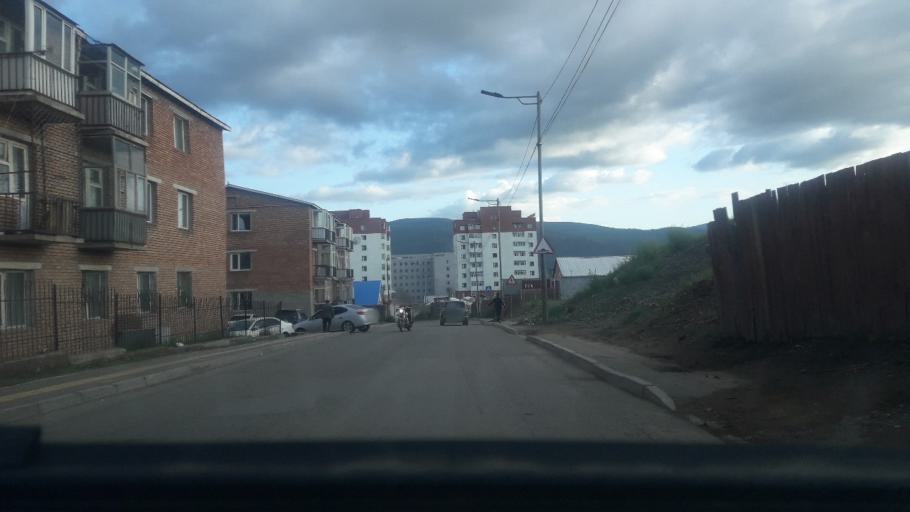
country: MN
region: Ulaanbaatar
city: Ulaanbaatar
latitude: 47.9192
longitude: 106.9954
